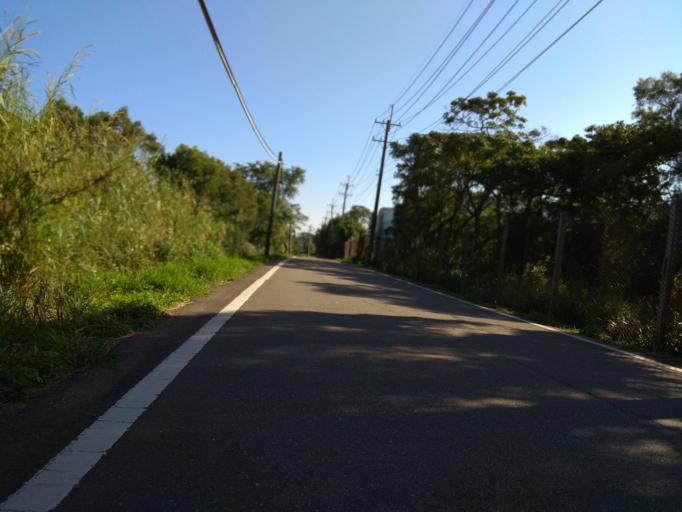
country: TW
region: Taiwan
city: Taoyuan City
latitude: 24.9737
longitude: 121.1772
